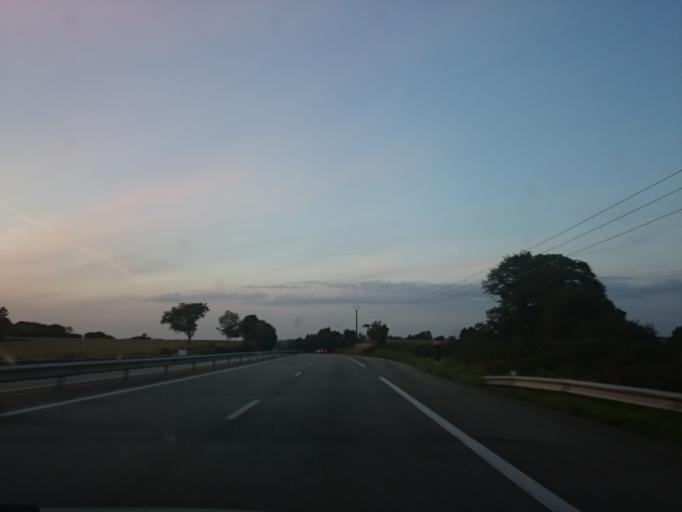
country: FR
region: Brittany
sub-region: Departement du Finistere
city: Briec
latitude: 48.1244
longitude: -4.0224
